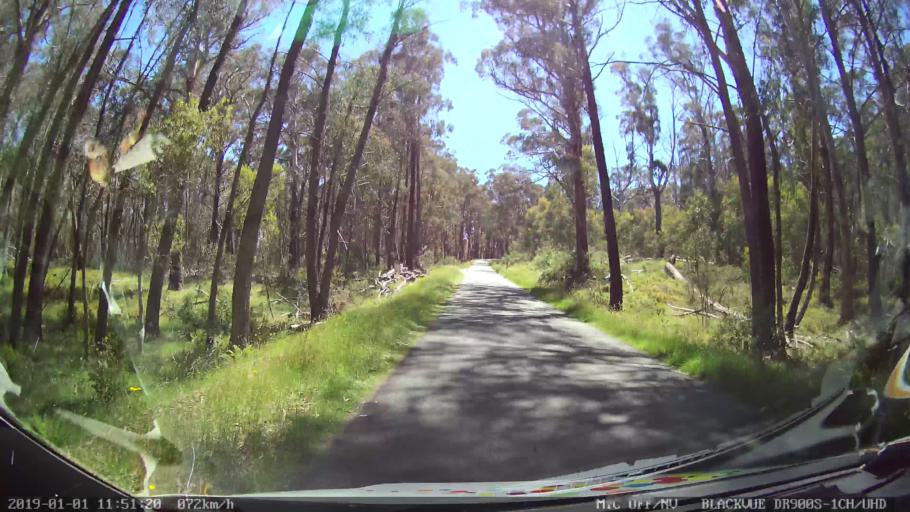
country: AU
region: New South Wales
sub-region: Snowy River
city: Jindabyne
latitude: -35.8861
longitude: 148.4292
